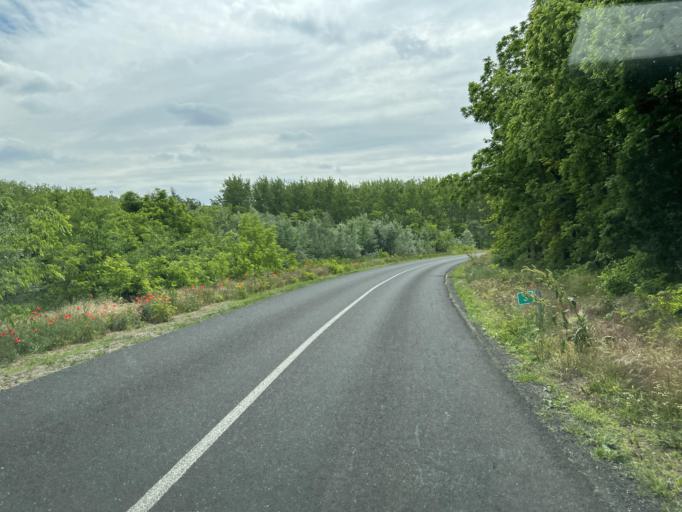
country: HU
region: Pest
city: Tapioszecso
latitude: 47.4753
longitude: 19.6156
